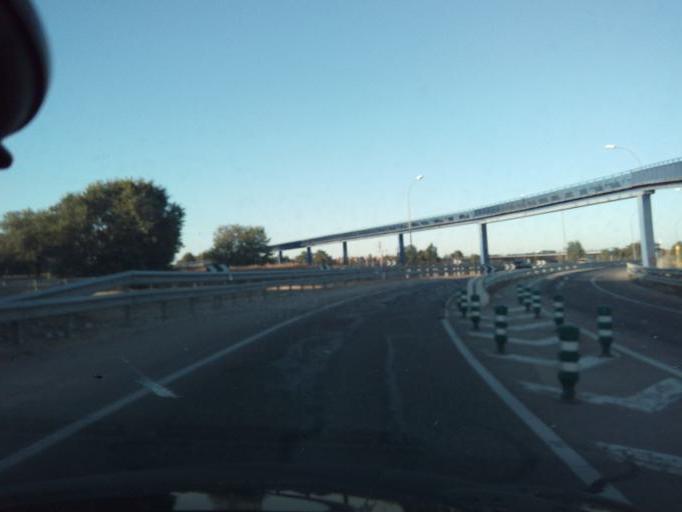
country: ES
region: Madrid
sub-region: Provincia de Madrid
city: Torrejon de Ardoz
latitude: 40.4672
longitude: -3.4851
